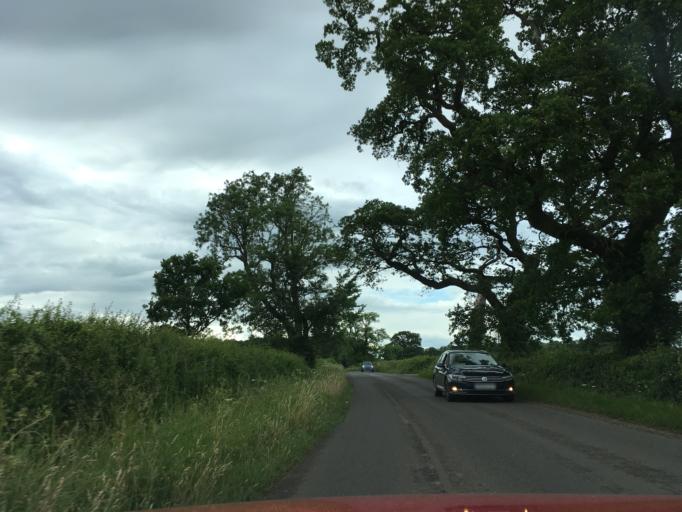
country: GB
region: England
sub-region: Wiltshire
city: Norton
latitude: 51.5954
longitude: -2.1804
